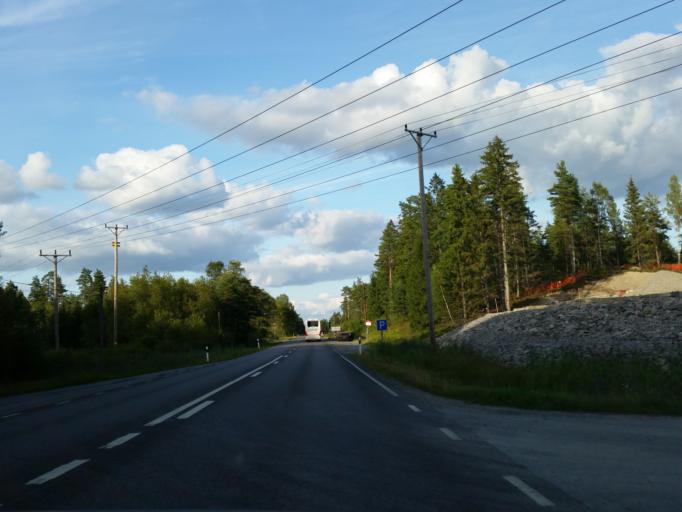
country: SE
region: Stockholm
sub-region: Sodertalje Kommun
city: Molnbo
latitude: 59.0666
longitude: 17.5253
